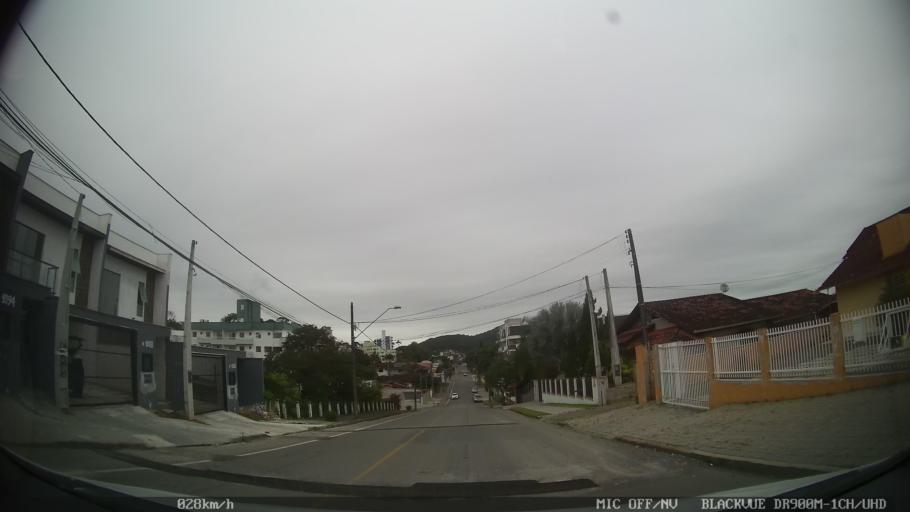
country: BR
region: Santa Catarina
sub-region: Joinville
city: Joinville
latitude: -26.2686
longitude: -48.8416
